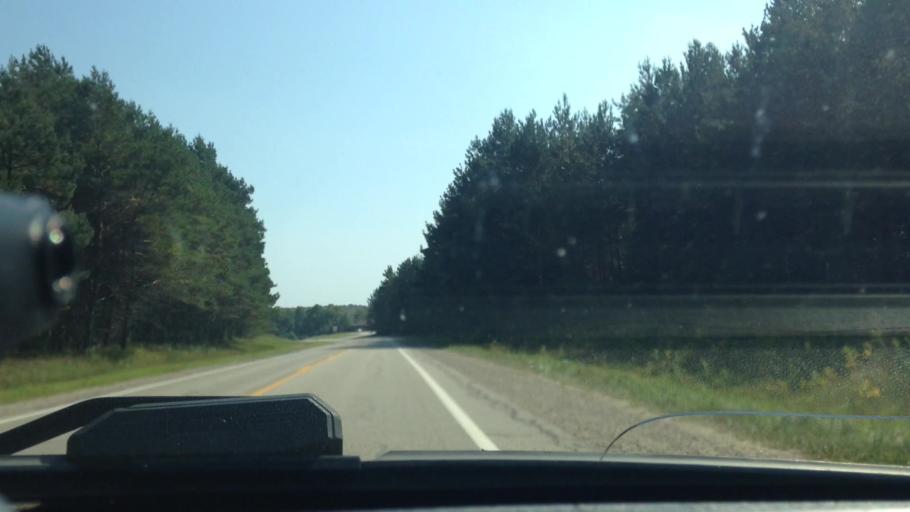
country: US
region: Michigan
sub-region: Luce County
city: Newberry
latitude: 46.3148
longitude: -85.6628
